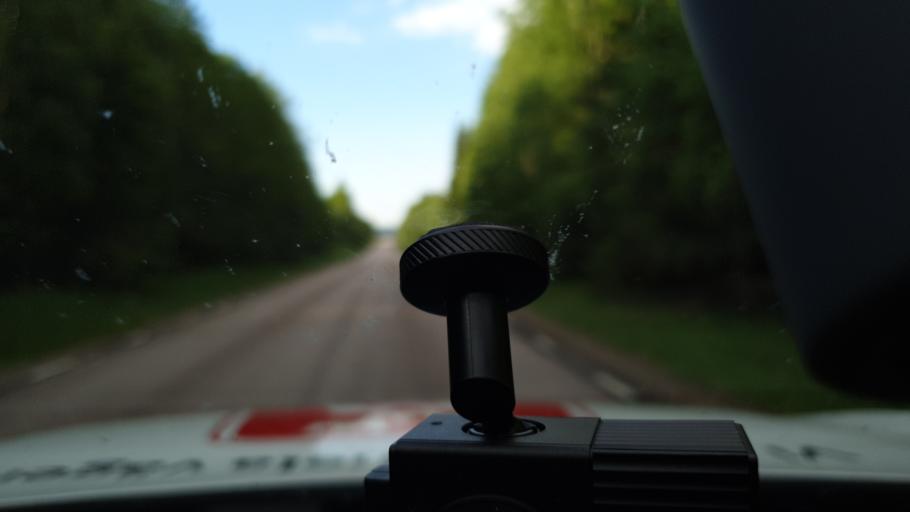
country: SE
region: Vaermland
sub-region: Torsby Kommun
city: Torsby
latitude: 60.0744
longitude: 12.9019
